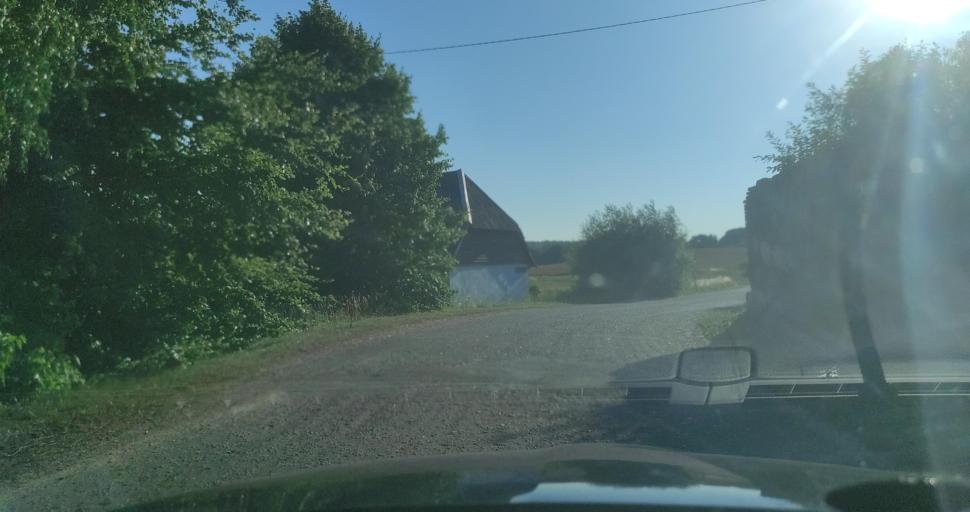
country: LV
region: Aizpute
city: Aizpute
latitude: 56.6973
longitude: 21.7982
